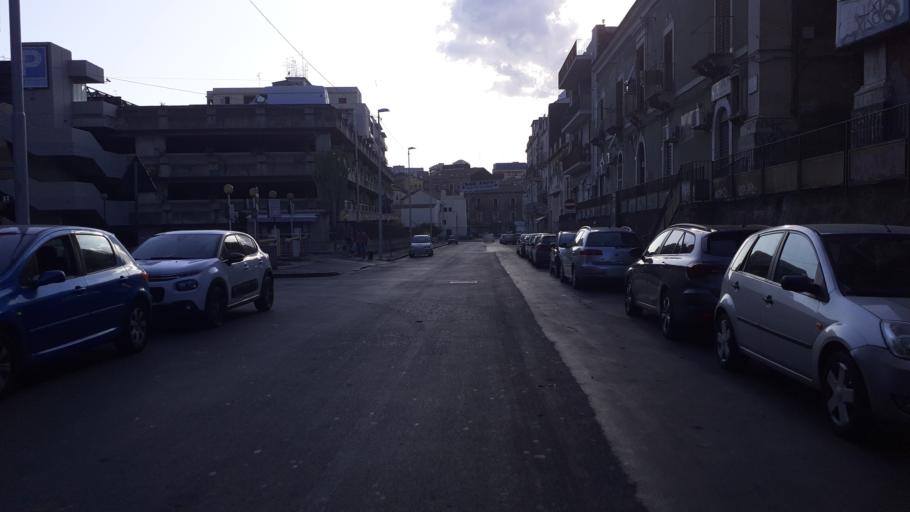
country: IT
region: Sicily
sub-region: Catania
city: Catania
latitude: 37.5089
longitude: 15.0902
